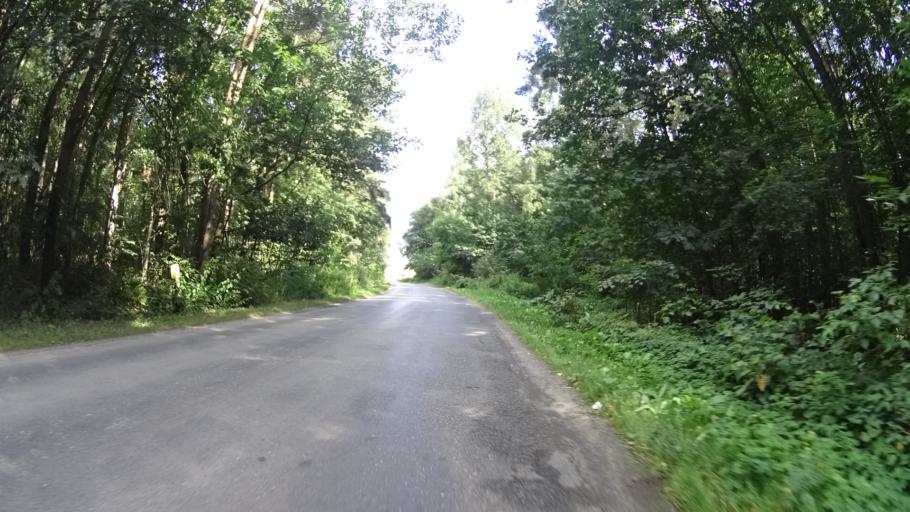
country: PL
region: Masovian Voivodeship
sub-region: Powiat grojecki
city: Mogielnica
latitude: 51.6917
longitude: 20.7390
